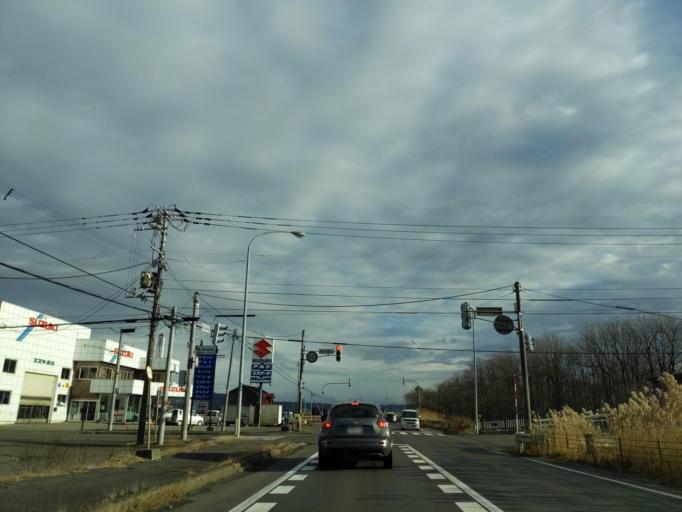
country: JP
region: Hokkaido
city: Kitahiroshima
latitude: 42.9627
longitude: 141.6832
